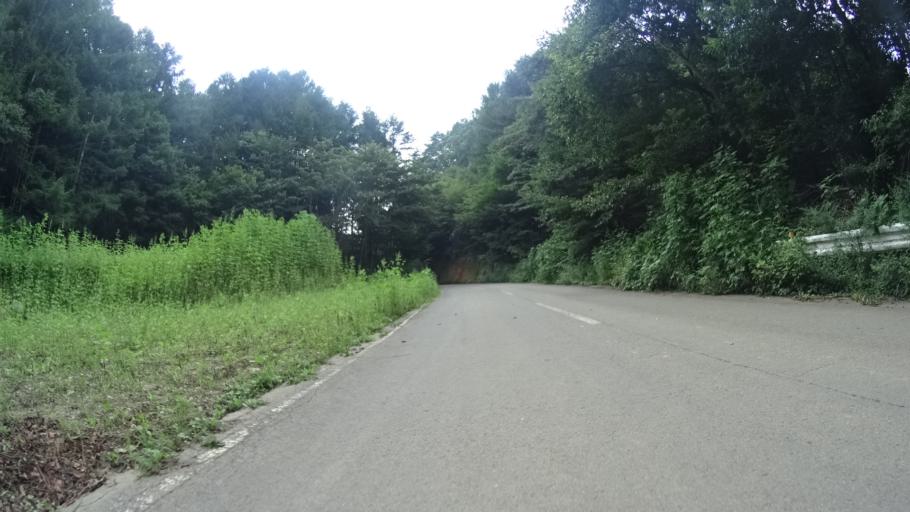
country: JP
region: Yamanashi
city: Nirasaki
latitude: 35.9063
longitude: 138.4663
